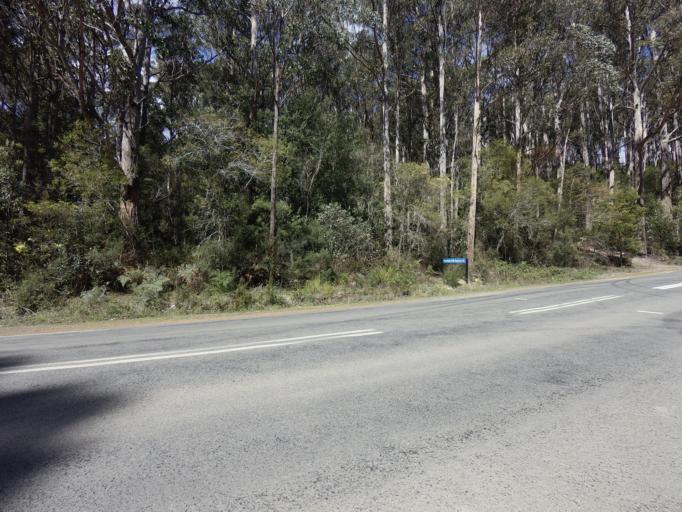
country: AU
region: Tasmania
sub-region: Derwent Valley
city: New Norfolk
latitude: -42.7274
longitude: 146.6738
